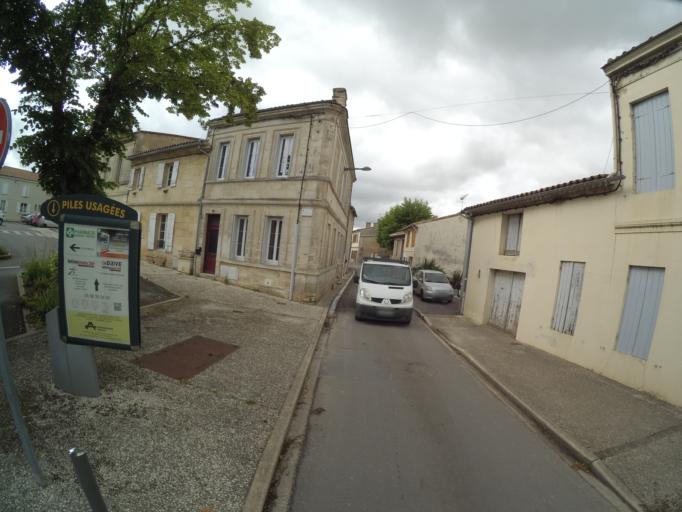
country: FR
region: Aquitaine
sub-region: Departement de la Gironde
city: Macau
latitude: 45.0090
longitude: -0.6124
